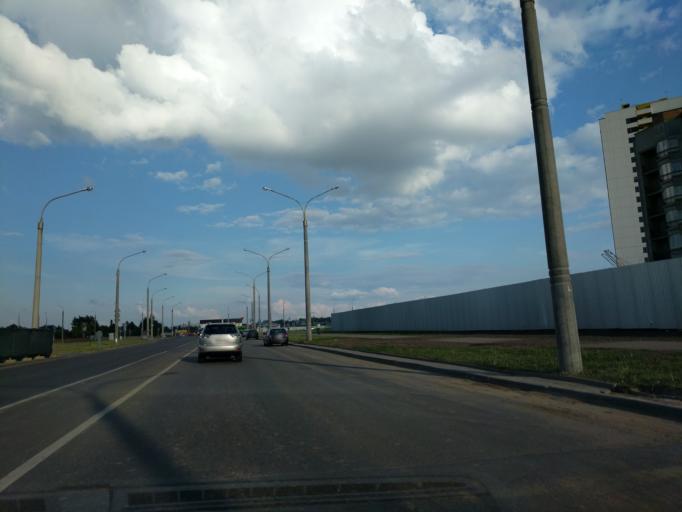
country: BY
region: Minsk
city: Zhdanovichy
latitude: 53.9319
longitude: 27.4428
